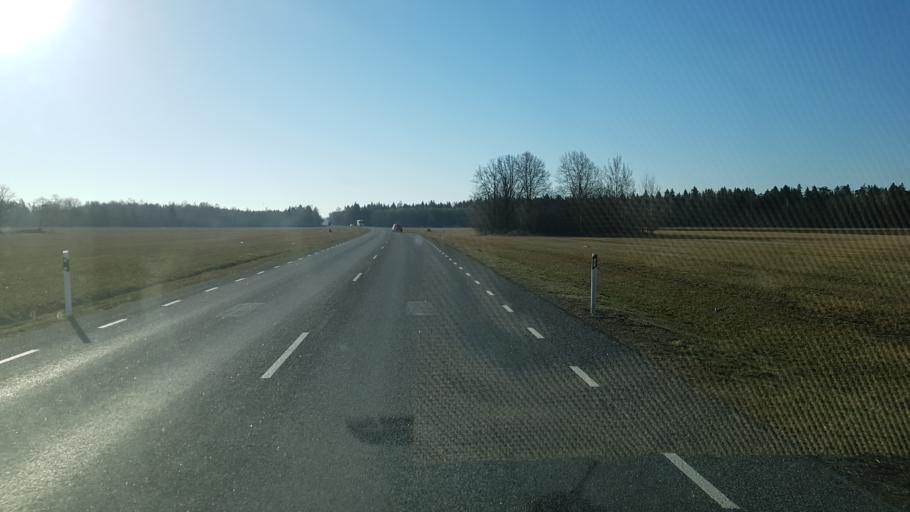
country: EE
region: Jaervamaa
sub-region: Tueri vald
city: Sarevere
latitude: 58.7697
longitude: 25.5234
